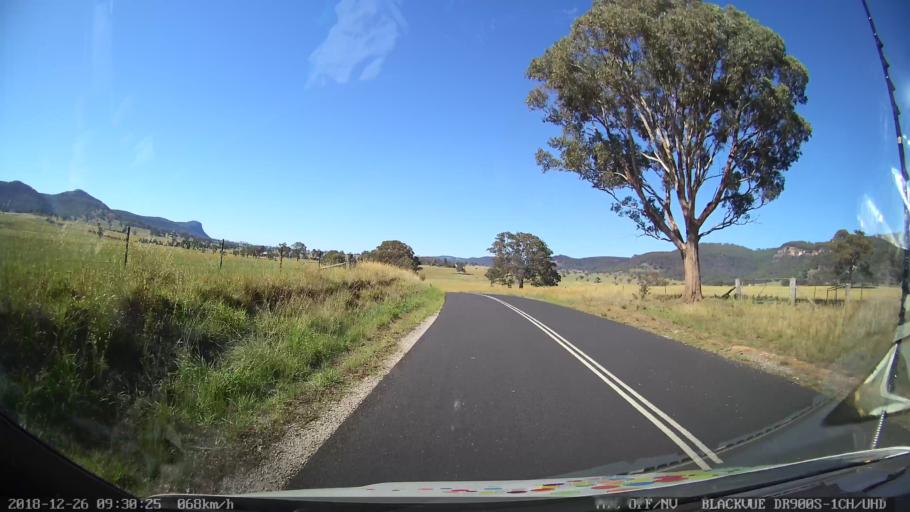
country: AU
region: New South Wales
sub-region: Mid-Western Regional
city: Kandos
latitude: -32.8627
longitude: 150.0290
